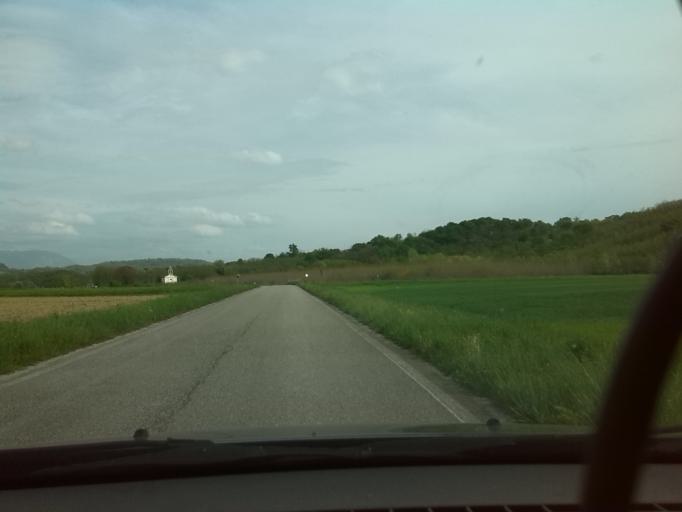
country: IT
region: Friuli Venezia Giulia
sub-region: Provincia di Gorizia
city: Capriva del Friuli
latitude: 45.9566
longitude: 13.5338
